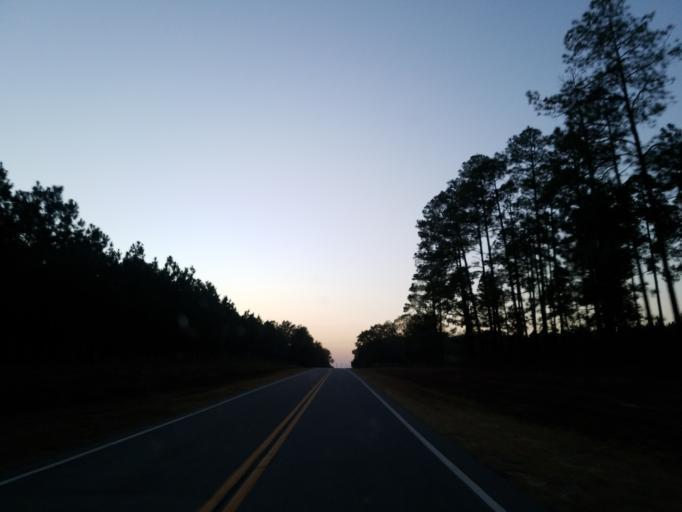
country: US
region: Georgia
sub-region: Turner County
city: Ashburn
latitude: 31.8239
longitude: -83.5535
